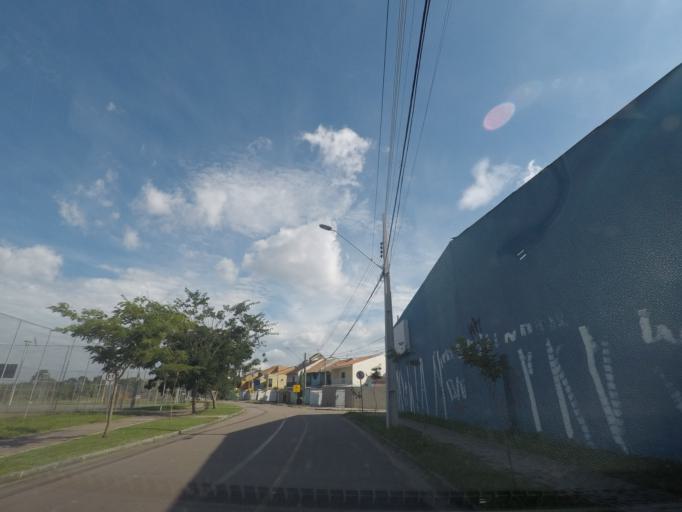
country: BR
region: Parana
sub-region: Curitiba
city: Curitiba
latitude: -25.4784
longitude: -49.3346
